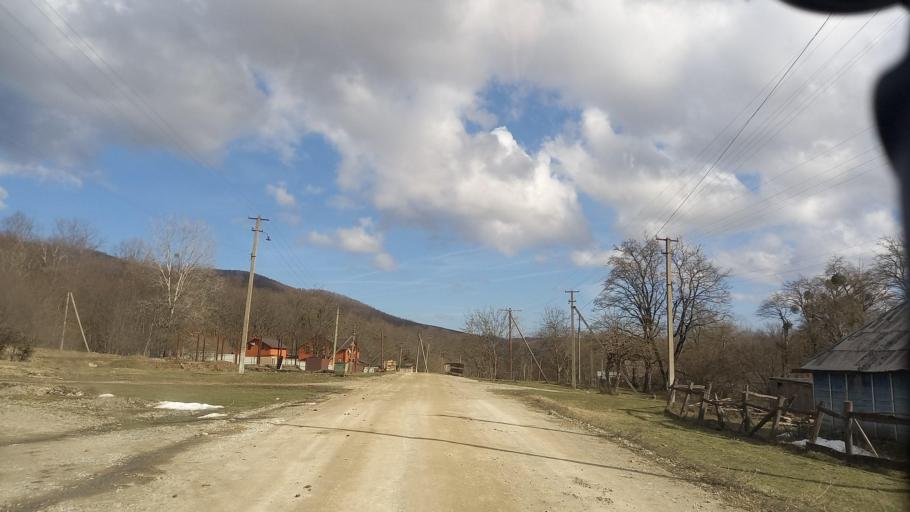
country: RU
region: Krasnodarskiy
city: Smolenskaya
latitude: 44.6028
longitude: 38.8606
